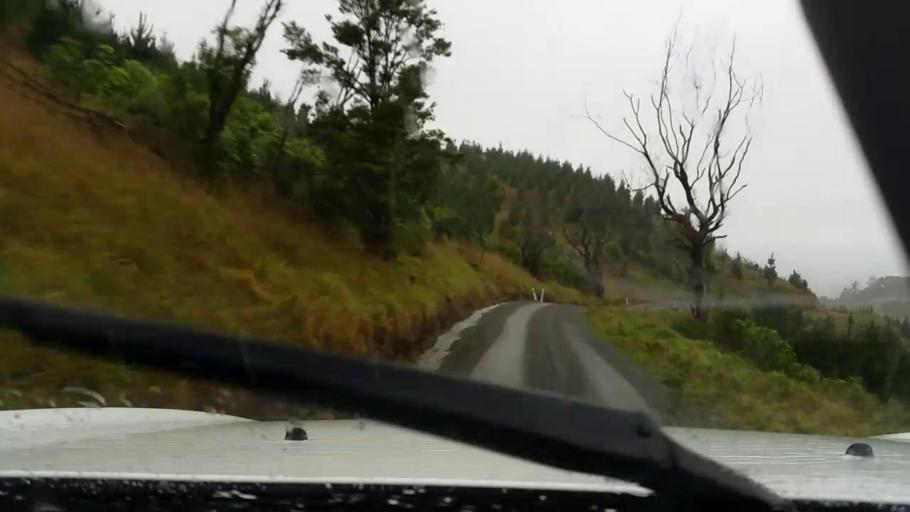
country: NZ
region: Wellington
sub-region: Masterton District
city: Masterton
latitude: -41.1963
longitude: 175.8112
